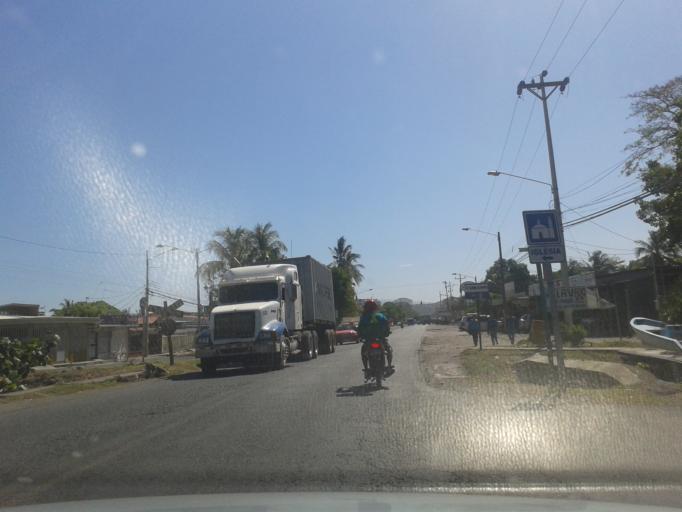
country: CR
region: Puntarenas
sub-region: Canton Central de Puntarenas
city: Chacarita
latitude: 9.9780
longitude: -84.7371
